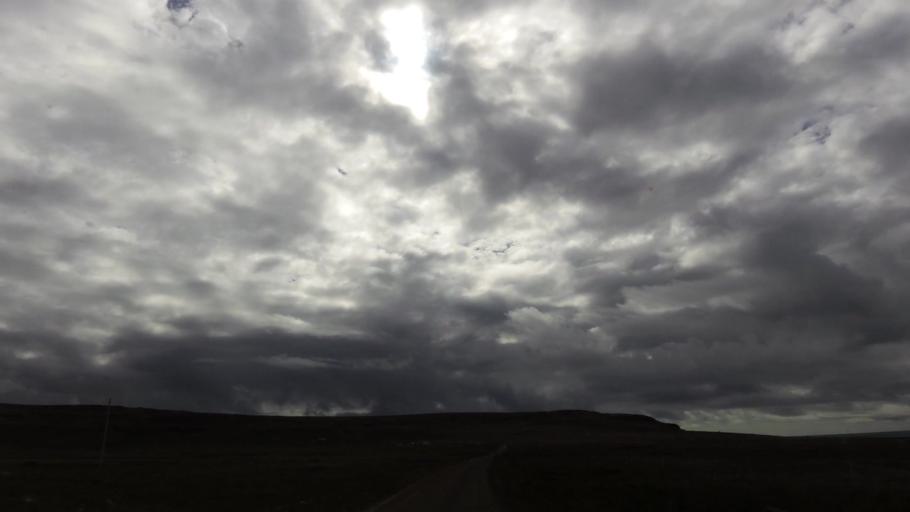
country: IS
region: West
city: Olafsvik
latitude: 65.6074
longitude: -24.3366
